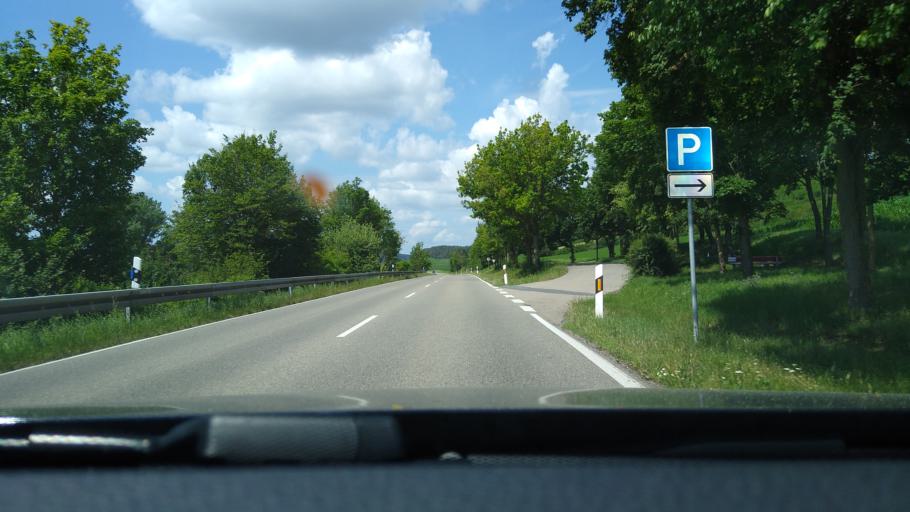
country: DE
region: Bavaria
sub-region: Regierungsbezirk Mittelfranken
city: Neuhof an der Zenn
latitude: 49.4577
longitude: 10.6334
